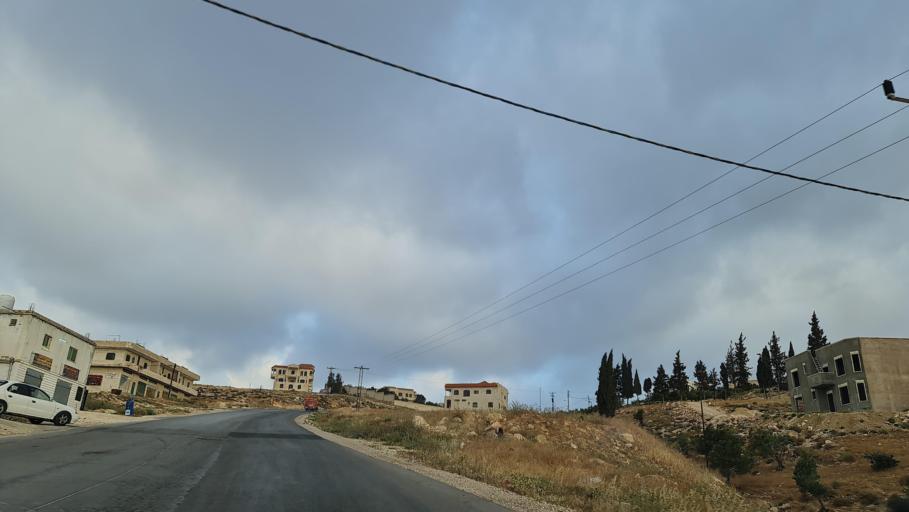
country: JO
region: Amman
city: Al Jubayhah
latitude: 32.0932
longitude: 35.9047
